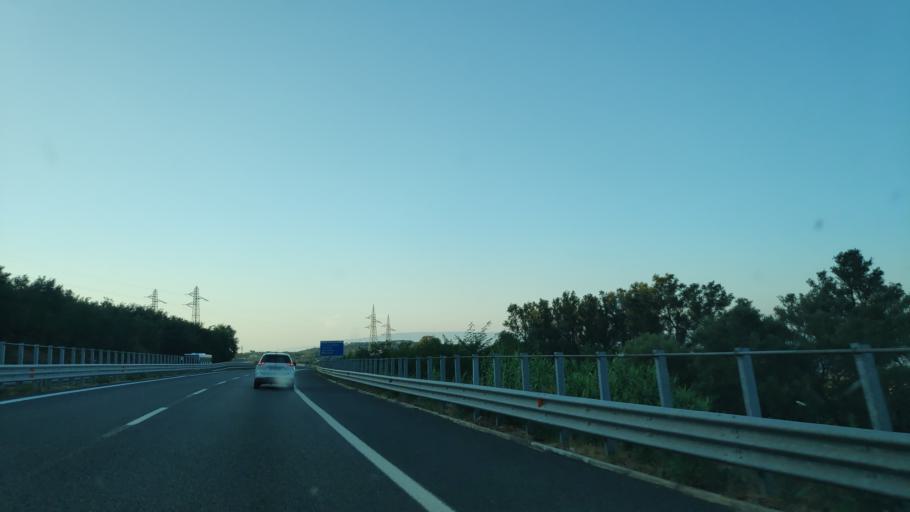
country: IT
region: Calabria
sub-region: Provincia di Reggio Calabria
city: Seminara
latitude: 38.3594
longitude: 15.8653
